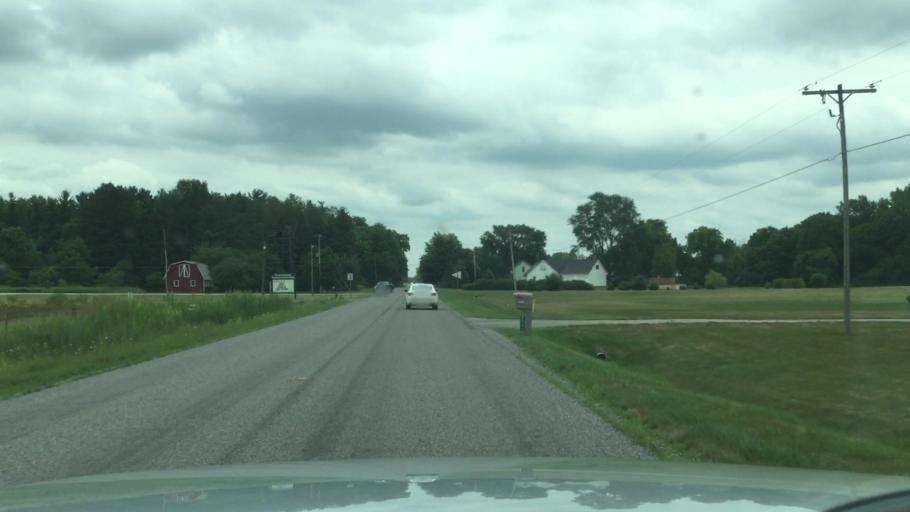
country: US
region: Michigan
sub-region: Saginaw County
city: Frankenmuth
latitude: 43.3217
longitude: -83.7891
